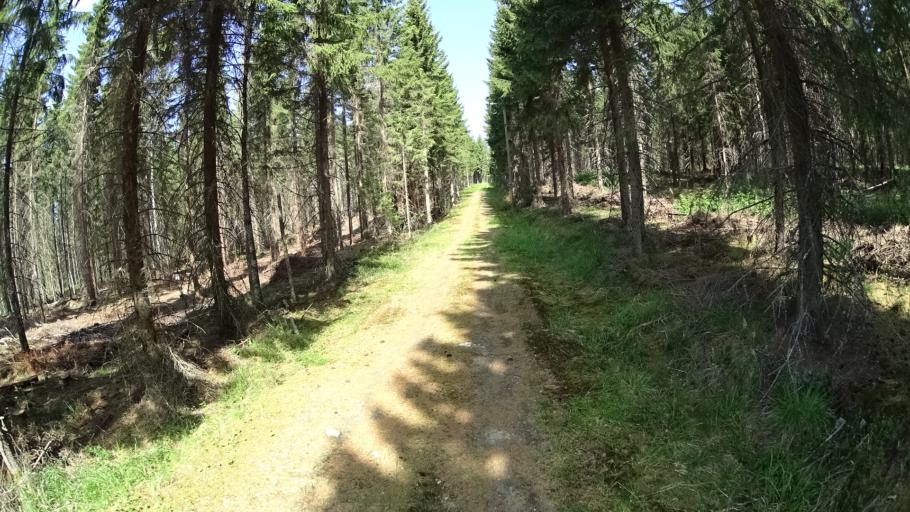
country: FI
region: North Karelia
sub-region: Pielisen Karjala
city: Lieksa
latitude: 63.1262
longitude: 29.7994
